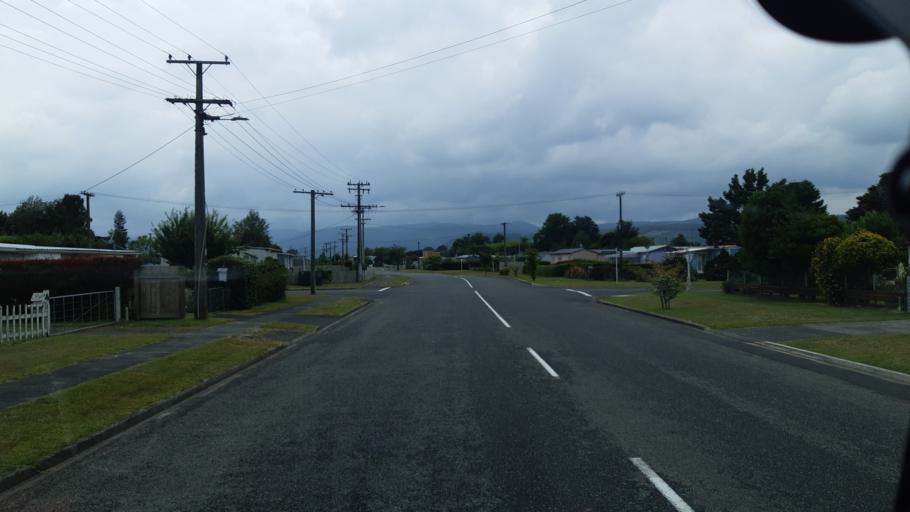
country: NZ
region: Waikato
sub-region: South Waikato District
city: Tokoroa
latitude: -38.3756
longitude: 175.7699
